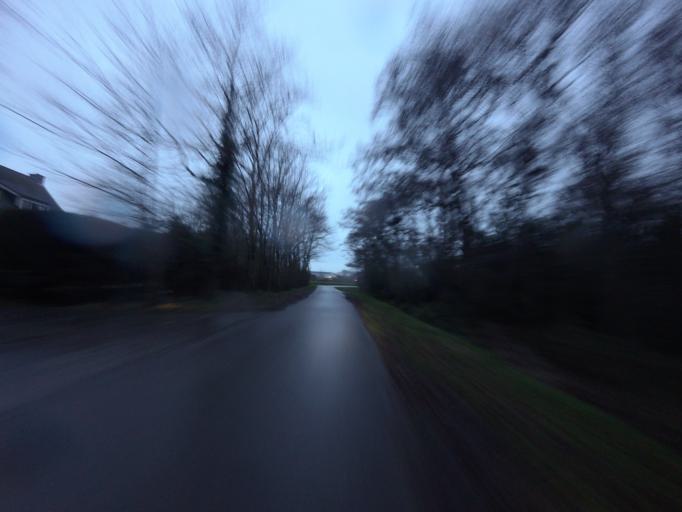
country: NL
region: North Holland
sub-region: Gemeente Texel
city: Den Burg
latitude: 53.0678
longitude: 4.7939
